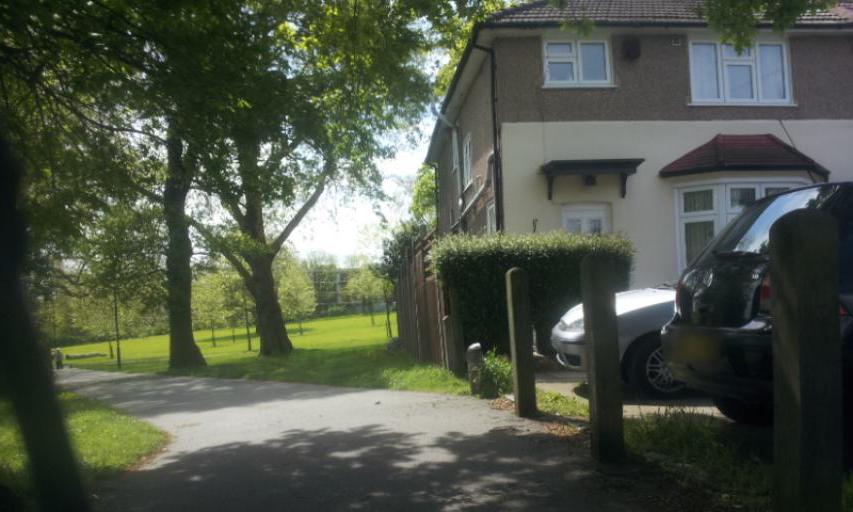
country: GB
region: England
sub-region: Greater London
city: Catford
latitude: 51.4493
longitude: -0.0287
